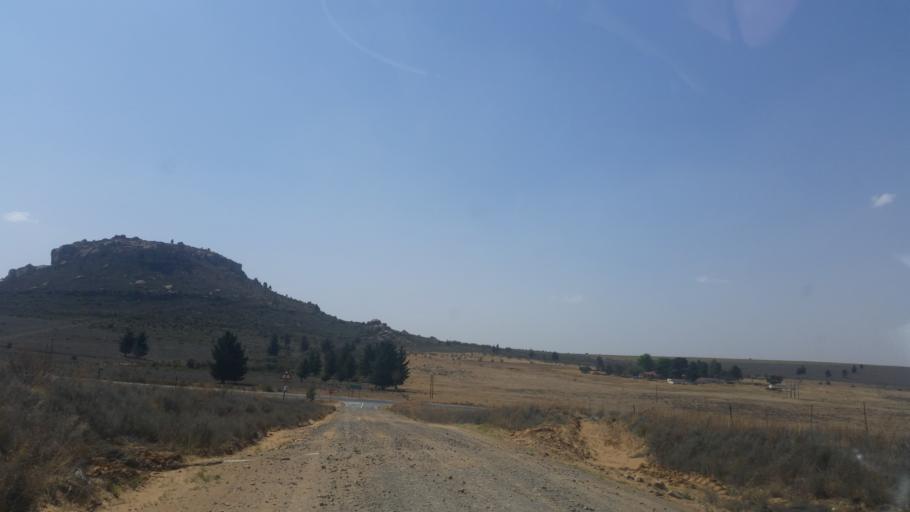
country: ZA
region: Orange Free State
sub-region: Thabo Mofutsanyana District Municipality
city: Bethlehem
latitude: -28.3065
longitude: 28.5718
